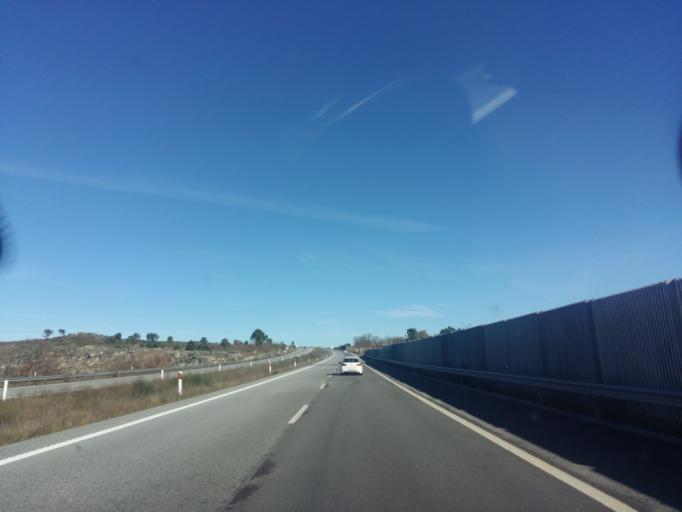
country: PT
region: Guarda
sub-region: Guarda
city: Sequeira
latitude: 40.5869
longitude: -7.1490
